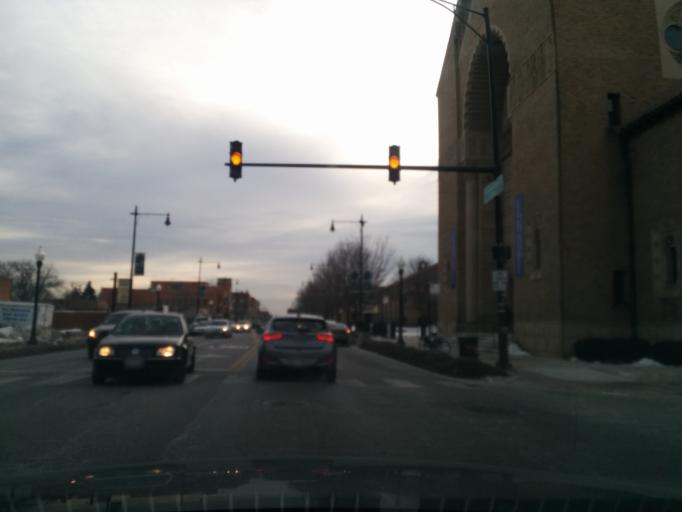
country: US
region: Illinois
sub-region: Cook County
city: Harwood Heights
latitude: 41.9529
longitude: -87.7817
